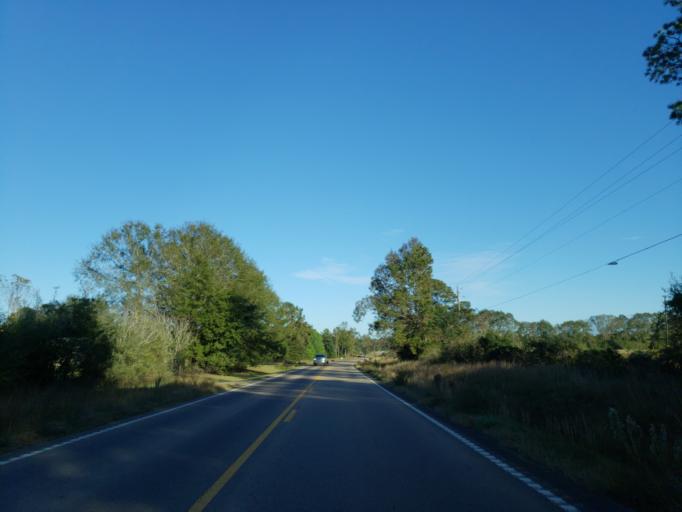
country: US
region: Mississippi
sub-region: Perry County
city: Richton
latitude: 31.3757
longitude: -88.8492
